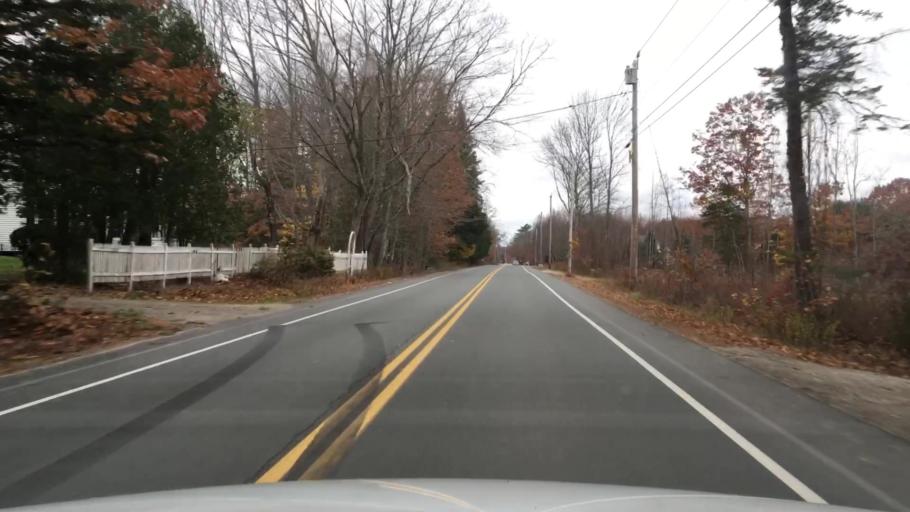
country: US
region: Maine
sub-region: Hancock County
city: Sedgwick
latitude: 44.4110
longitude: -68.6022
